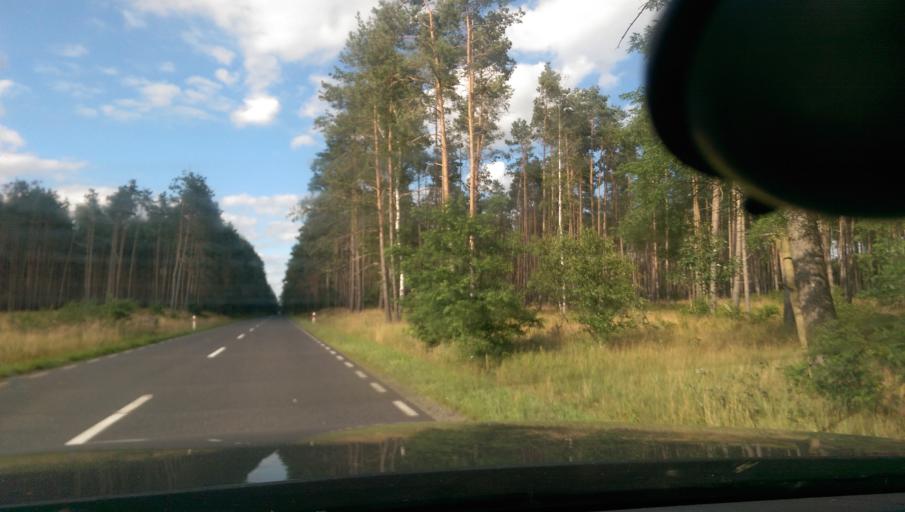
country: PL
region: Lubusz
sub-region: Powiat sulecinski
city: Krzeszyce
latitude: 52.5307
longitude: 14.9322
